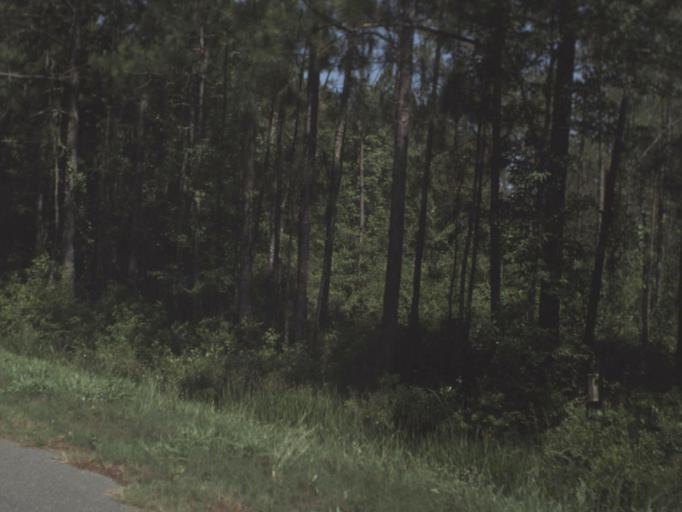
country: US
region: Florida
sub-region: Baker County
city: Macclenny
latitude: 30.2563
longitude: -82.2585
